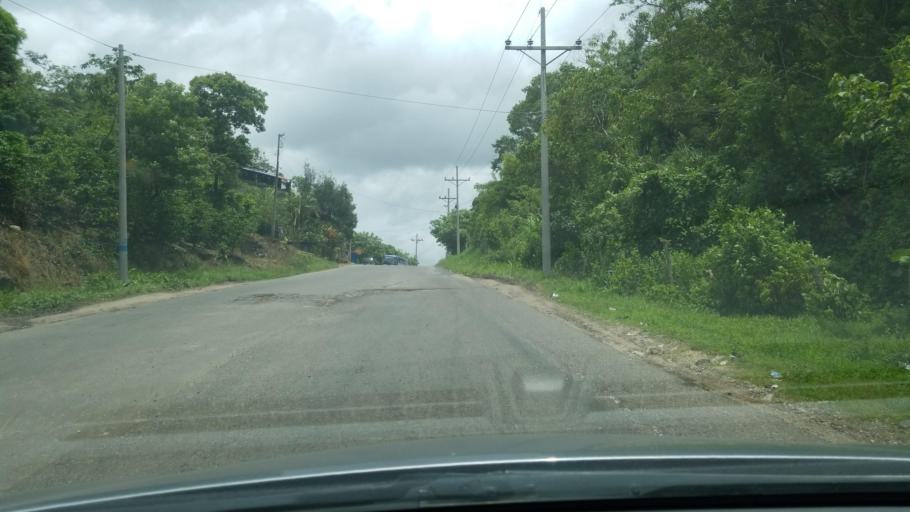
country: HN
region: Copan
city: Ojos de Agua
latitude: 14.6822
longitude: -88.8178
